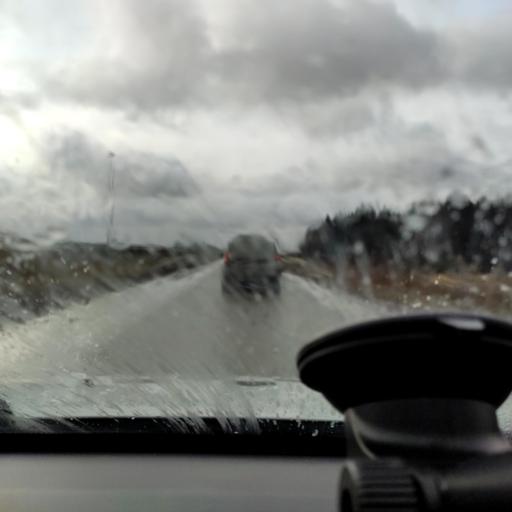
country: RU
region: Perm
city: Froly
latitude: 57.9348
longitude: 56.2663
